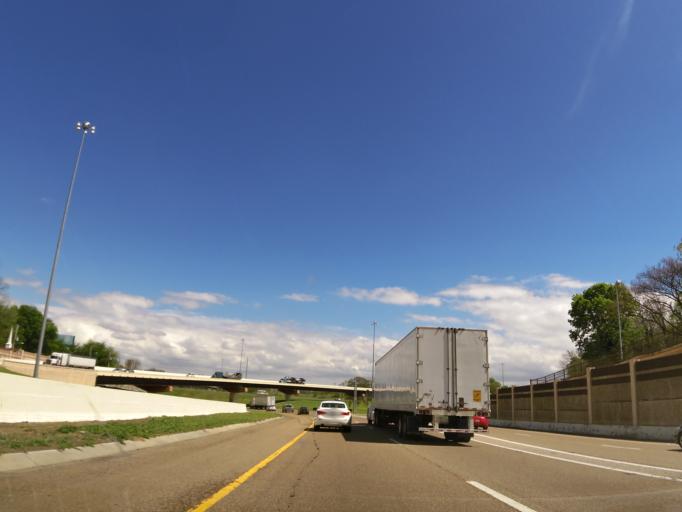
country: US
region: Tennessee
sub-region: Shelby County
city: Memphis
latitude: 35.1499
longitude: -90.0261
